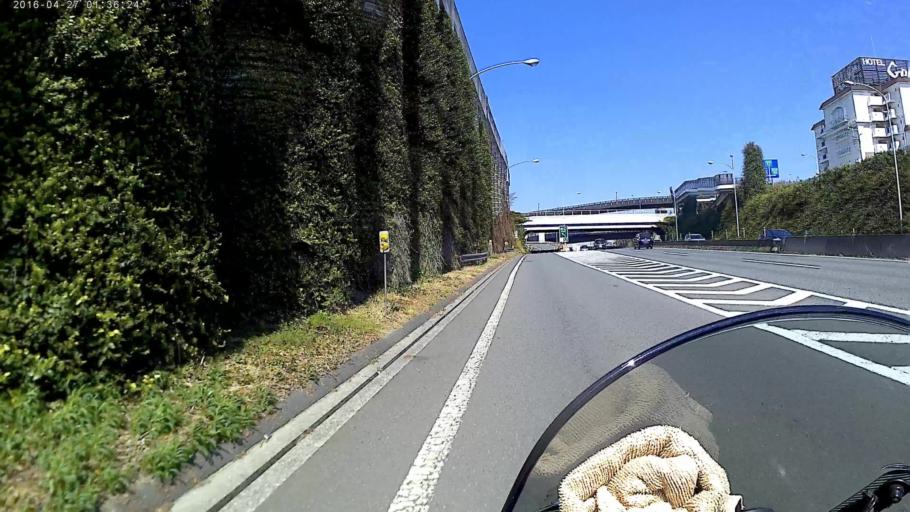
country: JP
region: Kanagawa
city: Yokohama
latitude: 35.4410
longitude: 139.5579
